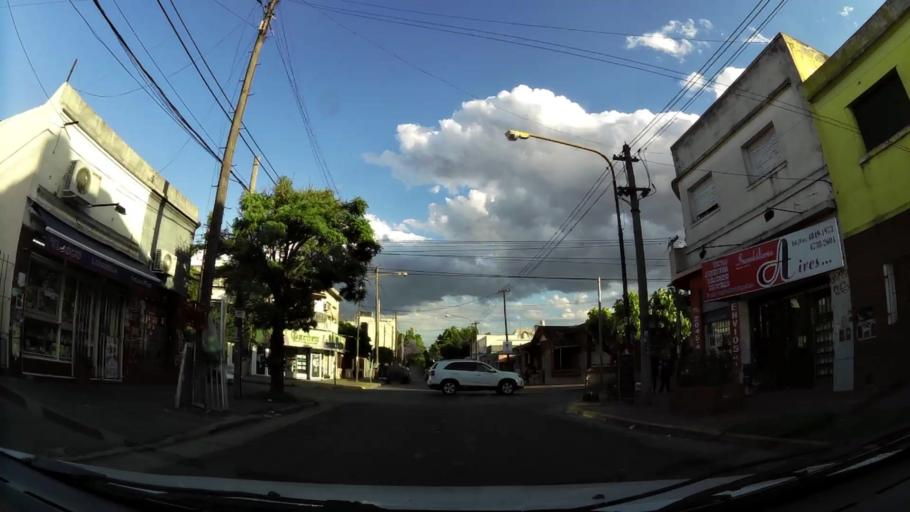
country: AR
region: Buenos Aires
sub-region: Partido de General San Martin
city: General San Martin
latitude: -34.5642
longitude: -58.5465
